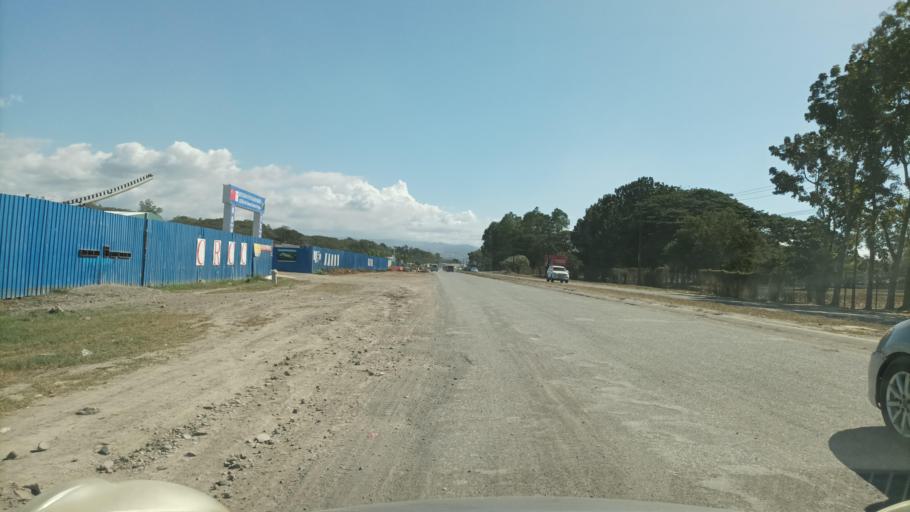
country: SB
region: Guadalcanal
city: Honiara
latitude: -9.4266
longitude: 160.0134
